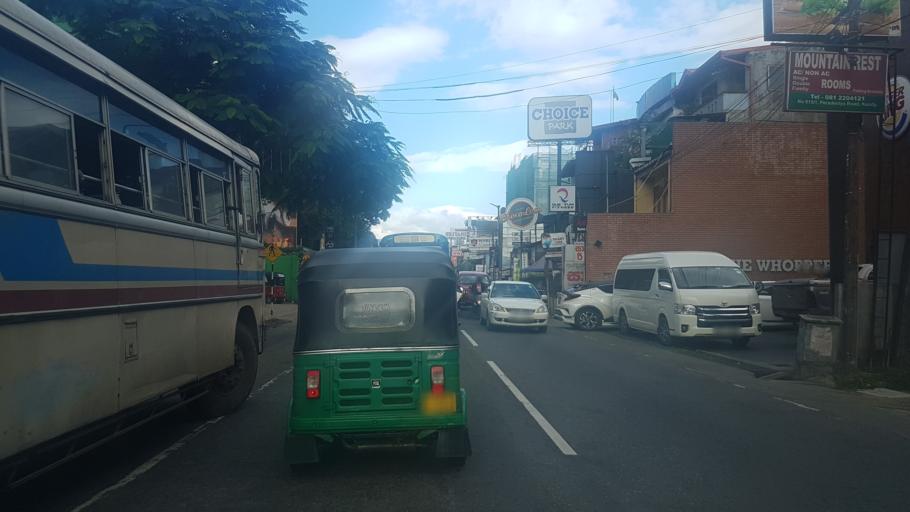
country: LK
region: Central
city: Kandy
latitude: 7.2822
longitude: 80.6218
